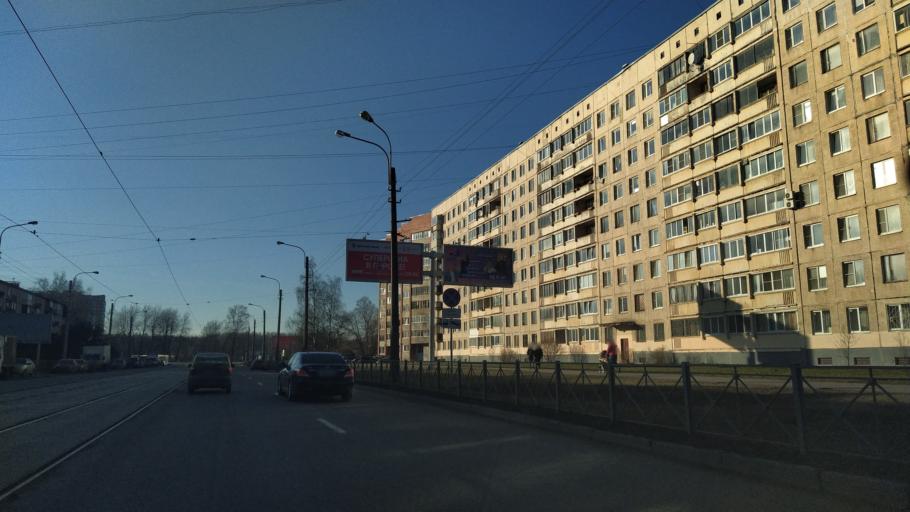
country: RU
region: Leningrad
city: Akademicheskoe
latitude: 60.0167
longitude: 30.3777
